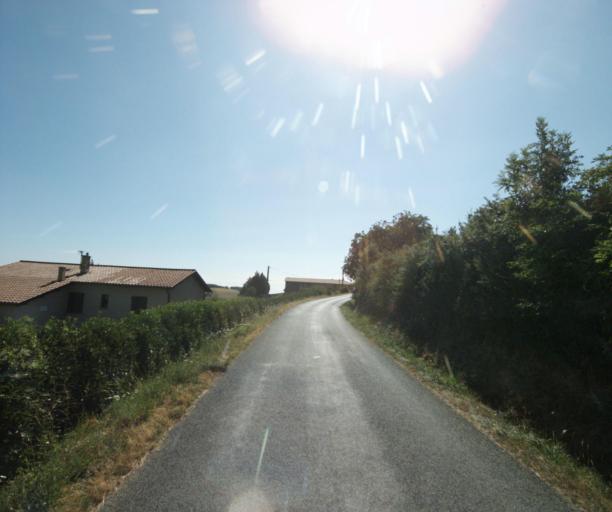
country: FR
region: Rhone-Alpes
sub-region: Departement du Rhone
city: Saint-Romain-de-Popey
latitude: 45.8246
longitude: 4.5325
